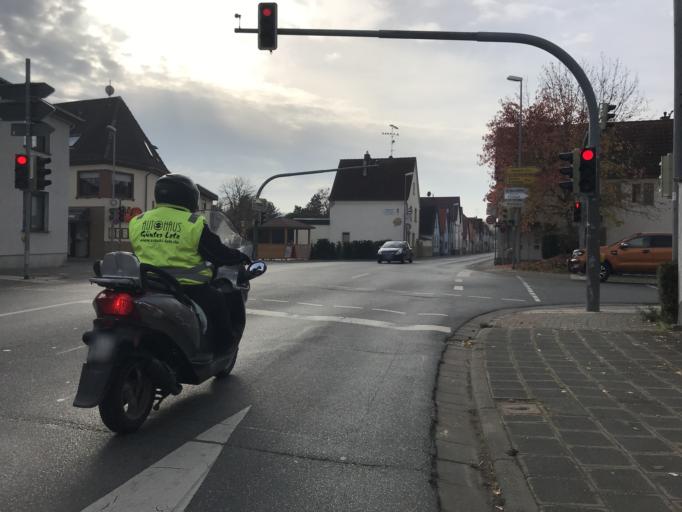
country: DE
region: Hesse
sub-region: Regierungsbezirk Darmstadt
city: Trebur
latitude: 49.9270
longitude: 8.4051
